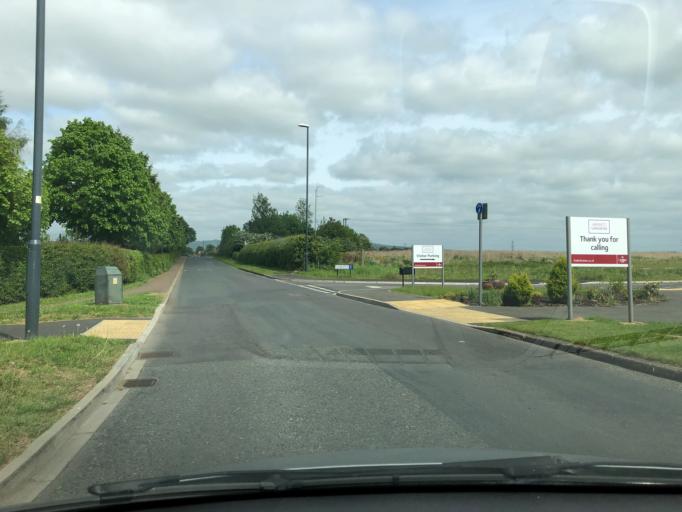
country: GB
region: England
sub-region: North Yorkshire
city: Thirsk
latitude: 54.2210
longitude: -1.3500
